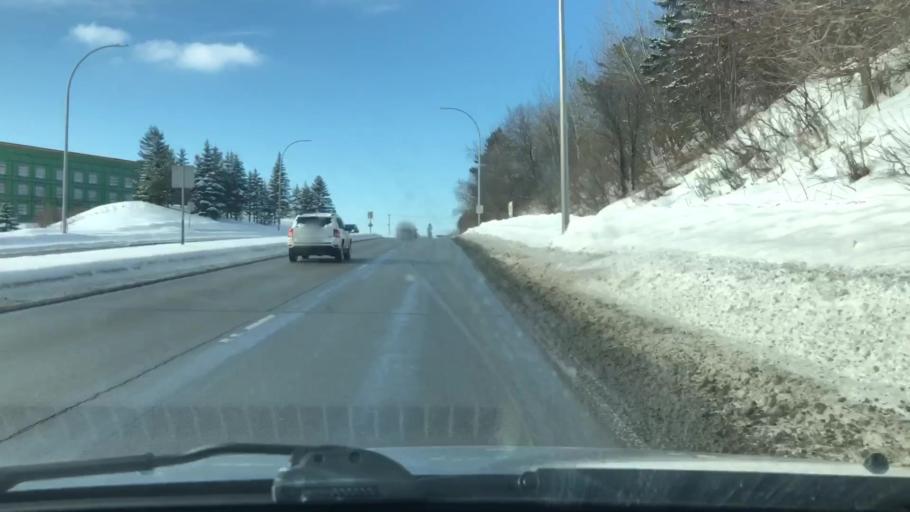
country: US
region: Minnesota
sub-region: Saint Louis County
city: Duluth
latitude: 46.7997
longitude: -92.1178
